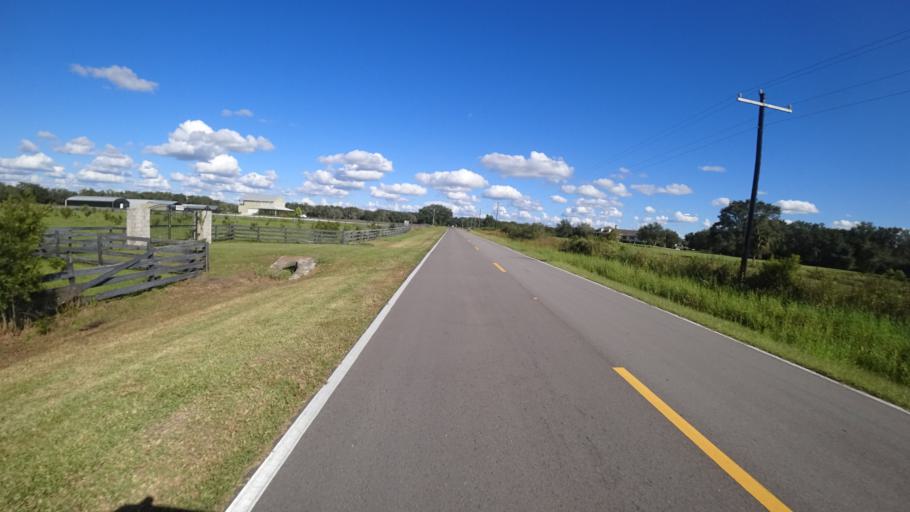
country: US
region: Florida
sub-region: Sarasota County
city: Lake Sarasota
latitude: 27.2889
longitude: -82.2227
